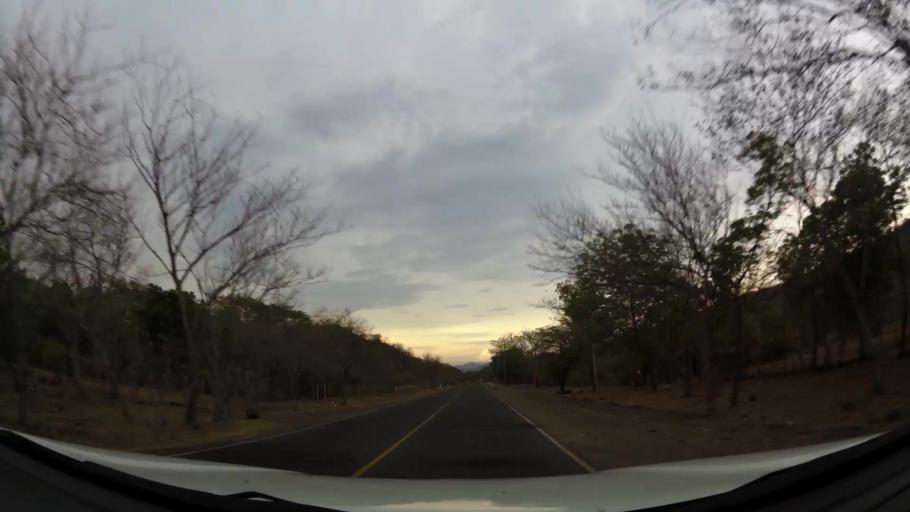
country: NI
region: Leon
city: La Jicaral
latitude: 12.7003
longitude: -86.4013
